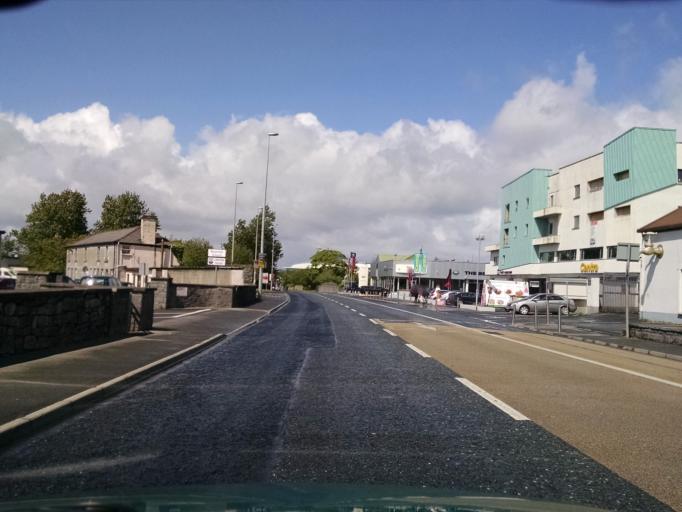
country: IE
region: Connaught
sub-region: County Galway
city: Gaillimh
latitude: 53.2800
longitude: -9.0256
